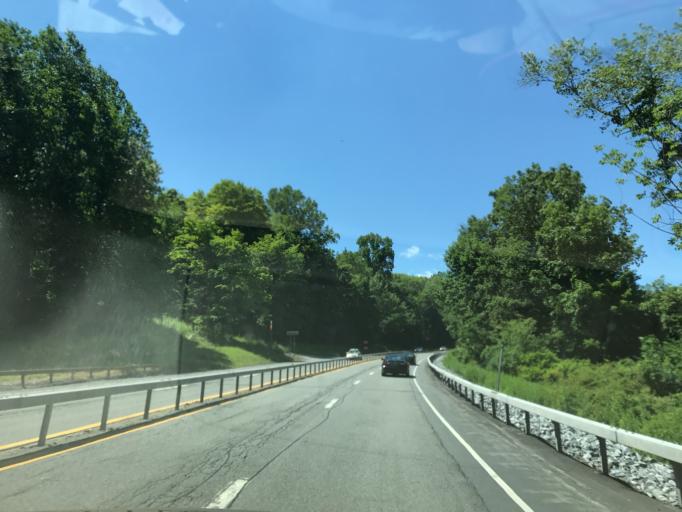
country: US
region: New York
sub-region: Dutchess County
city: Brinckerhoff
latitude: 41.5000
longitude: -73.7960
